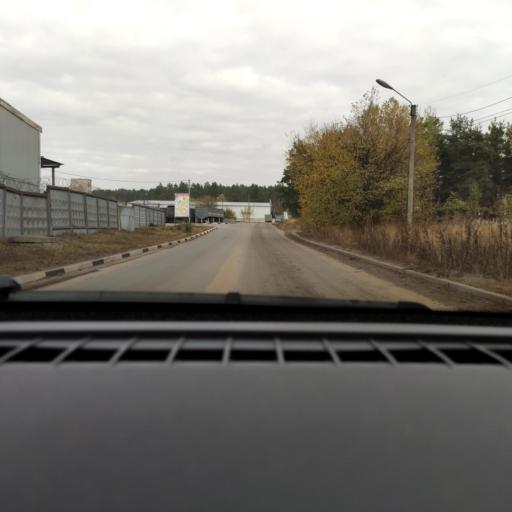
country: RU
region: Voronezj
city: Pridonskoy
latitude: 51.6398
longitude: 39.1105
